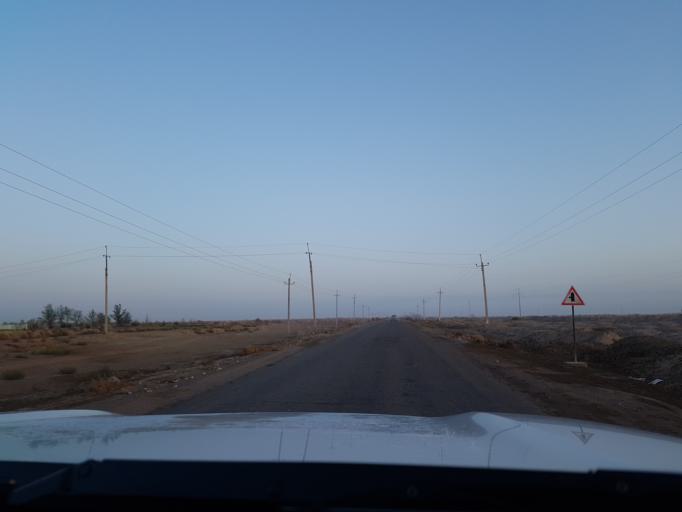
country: TM
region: Dasoguz
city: Koeneuergench
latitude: 41.8188
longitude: 58.7034
